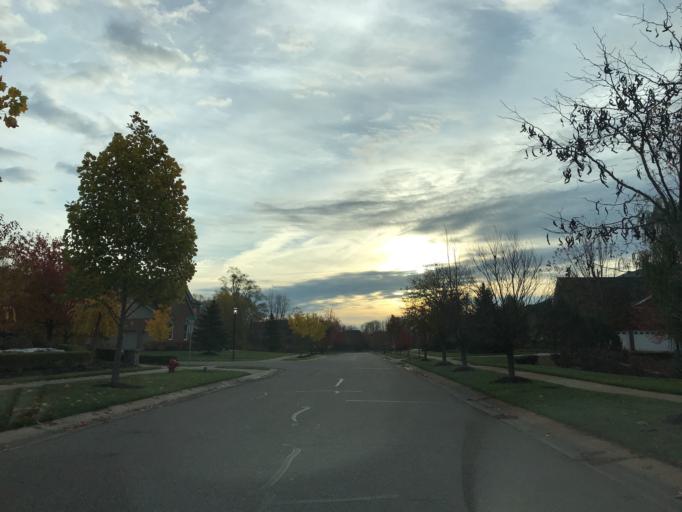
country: US
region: Michigan
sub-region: Oakland County
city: Wixom
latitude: 42.4779
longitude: -83.5430
